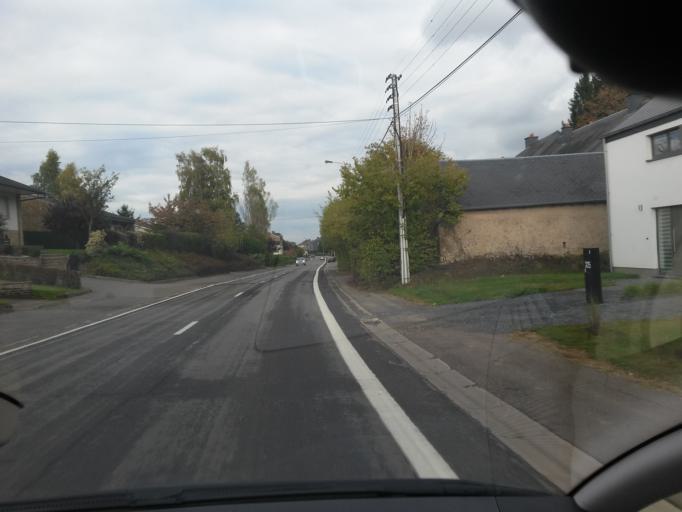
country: BE
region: Wallonia
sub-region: Province du Luxembourg
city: Arlon
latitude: 49.6968
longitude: 5.8206
